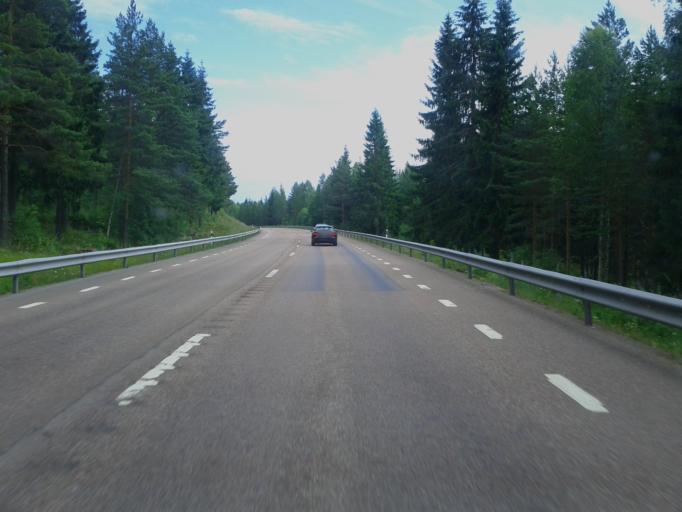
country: SE
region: Dalarna
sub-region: Faluns Kommun
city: Grycksbo
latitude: 60.7049
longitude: 15.4673
